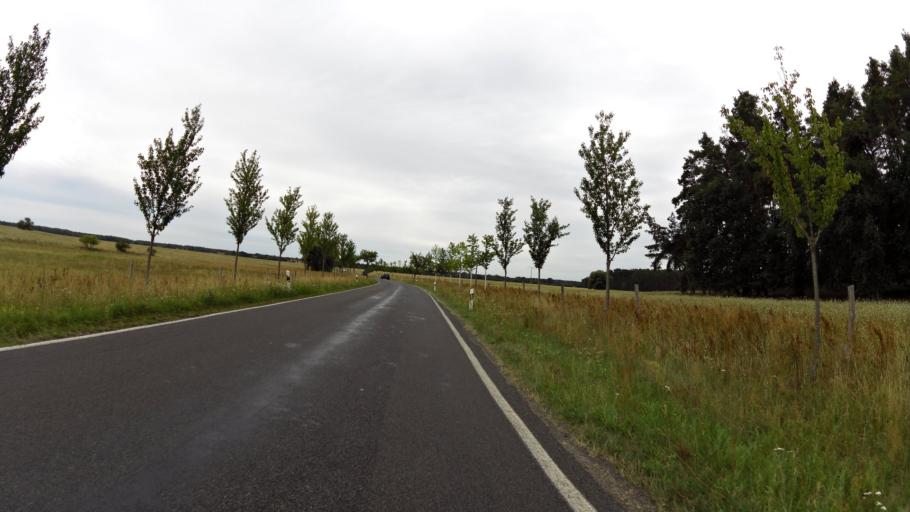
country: DE
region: Brandenburg
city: Wendisch Rietz
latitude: 52.1811
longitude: 14.0601
